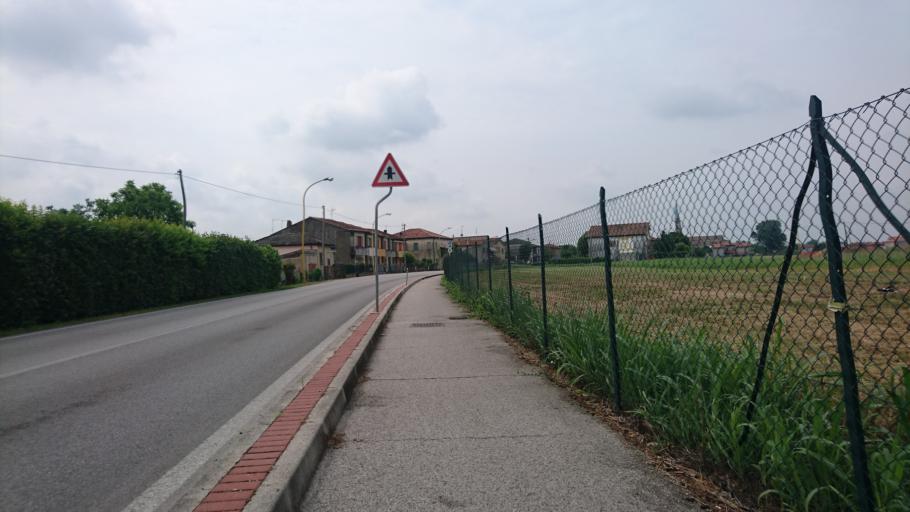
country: IT
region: Veneto
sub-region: Provincia di Padova
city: Villa Estense
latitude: 45.1769
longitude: 11.6708
